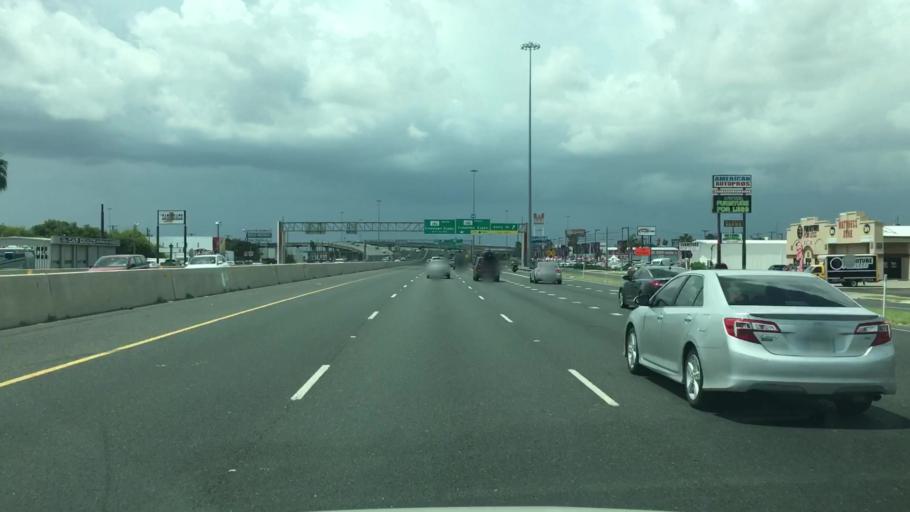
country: US
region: Texas
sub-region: Nueces County
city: Corpus Christi
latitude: 27.7330
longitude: -97.4219
